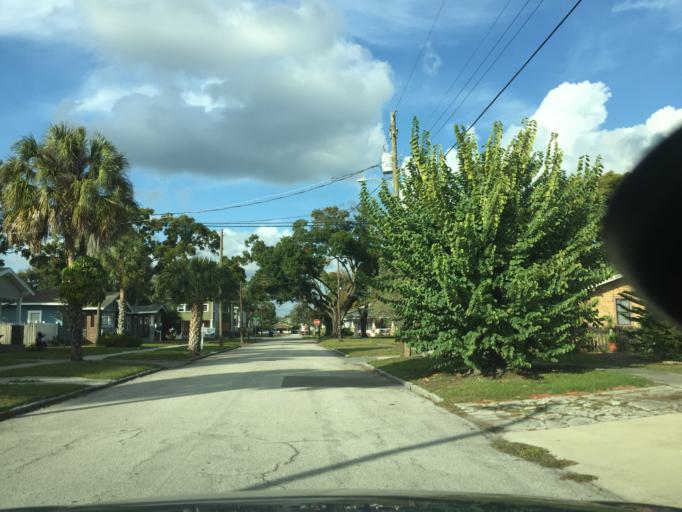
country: US
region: Florida
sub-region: Hillsborough County
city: Tampa
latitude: 27.9462
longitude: -82.4866
